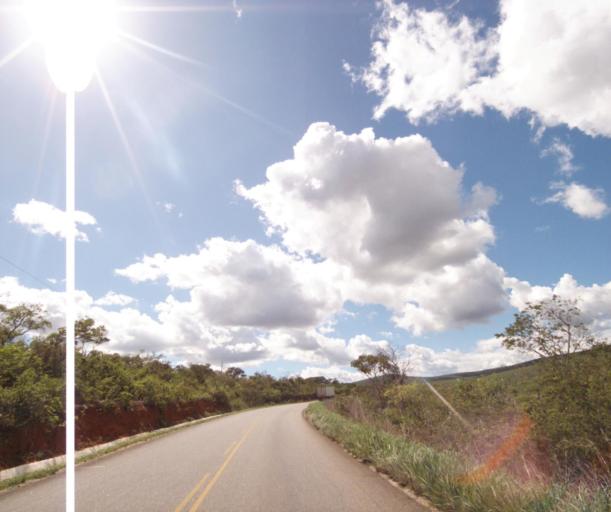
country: BR
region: Bahia
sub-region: Caetite
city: Caetite
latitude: -14.1517
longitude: -42.3544
